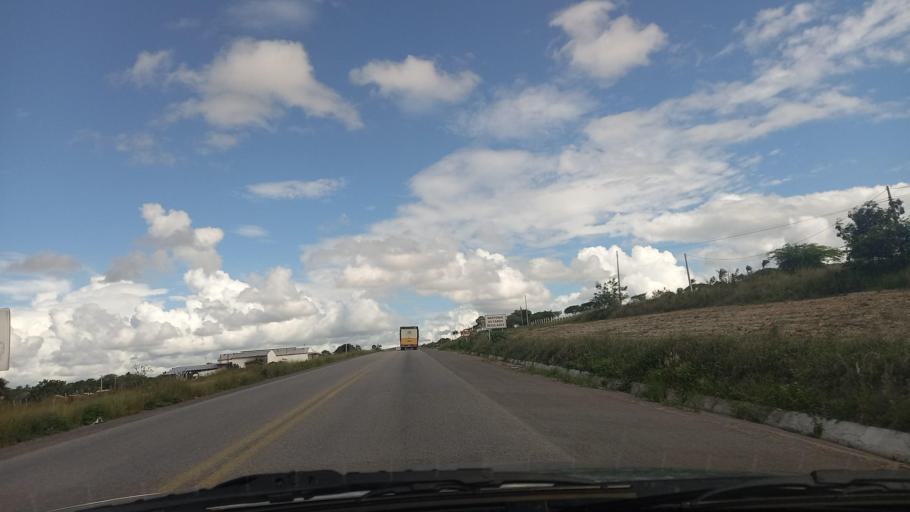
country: BR
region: Pernambuco
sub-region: Sao Joao
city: Sao Joao
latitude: -8.7586
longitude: -36.4305
